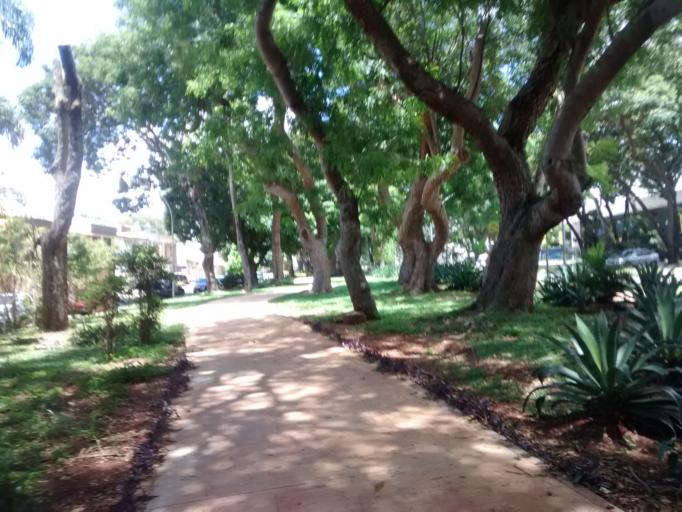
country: BR
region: Federal District
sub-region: Brasilia
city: Brasilia
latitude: -15.8027
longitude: -47.8991
